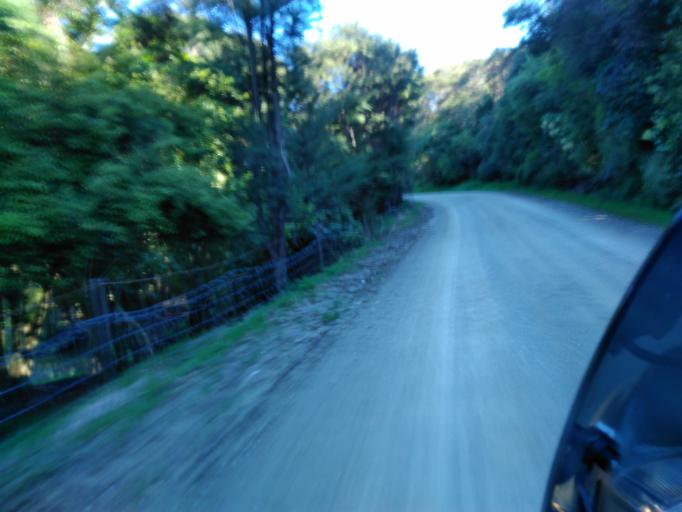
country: NZ
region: Gisborne
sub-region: Gisborne District
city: Gisborne
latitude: -38.3987
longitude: 177.6782
